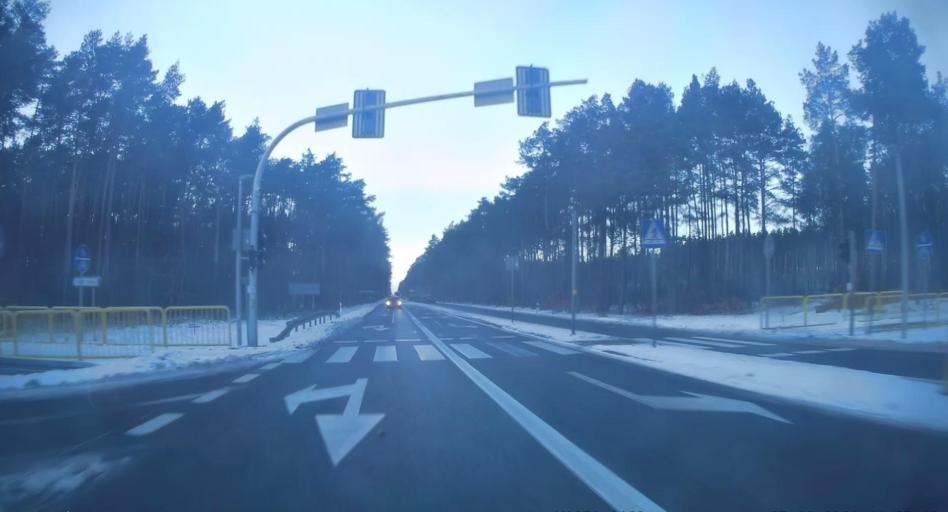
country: PL
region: Swietokrzyskie
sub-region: Powiat konecki
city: Ruda Maleniecka
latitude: 51.1448
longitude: 20.2441
